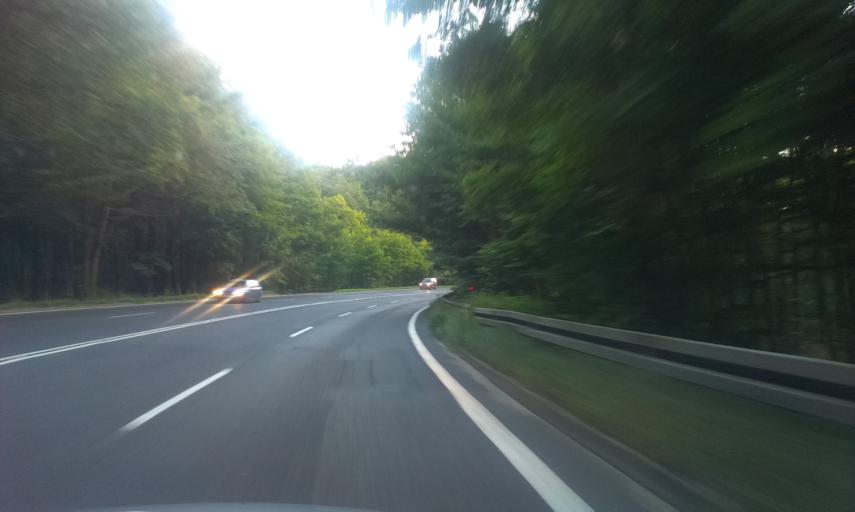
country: PL
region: West Pomeranian Voivodeship
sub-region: Koszalin
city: Koszalin
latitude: 54.2114
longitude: 16.2184
